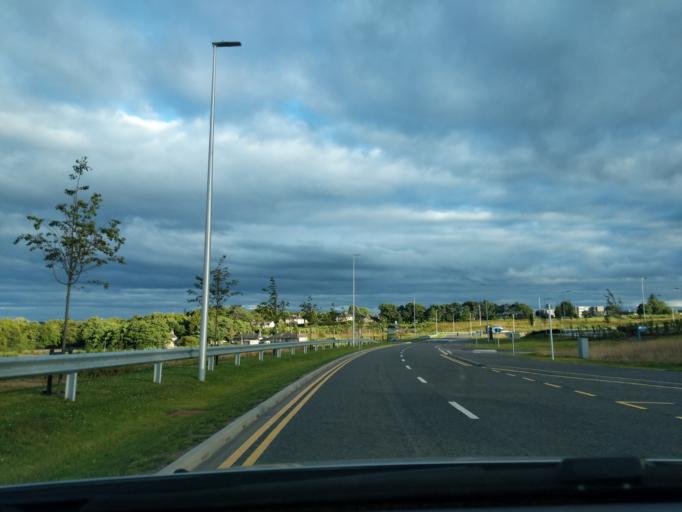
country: GB
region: Scotland
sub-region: Aberdeen City
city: Dyce
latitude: 57.1868
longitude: -2.1878
